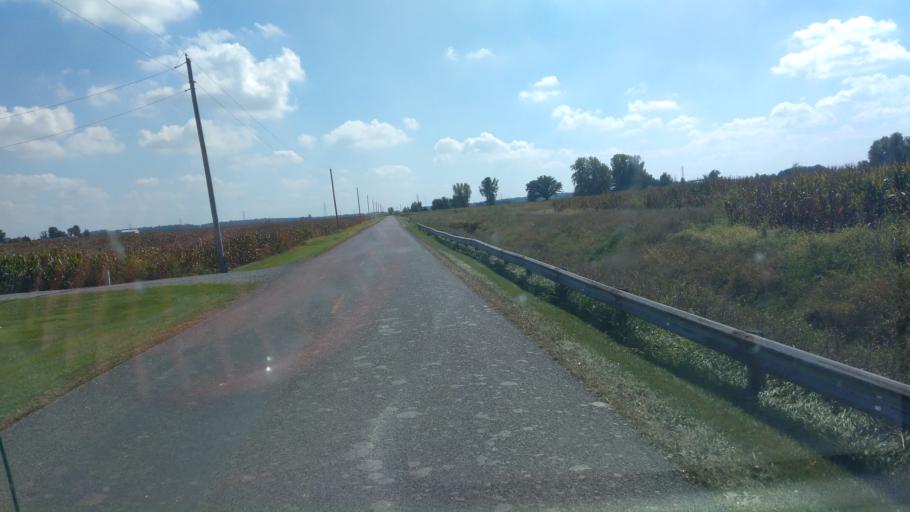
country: US
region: Ohio
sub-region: Hardin County
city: Ada
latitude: 40.6823
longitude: -83.8421
